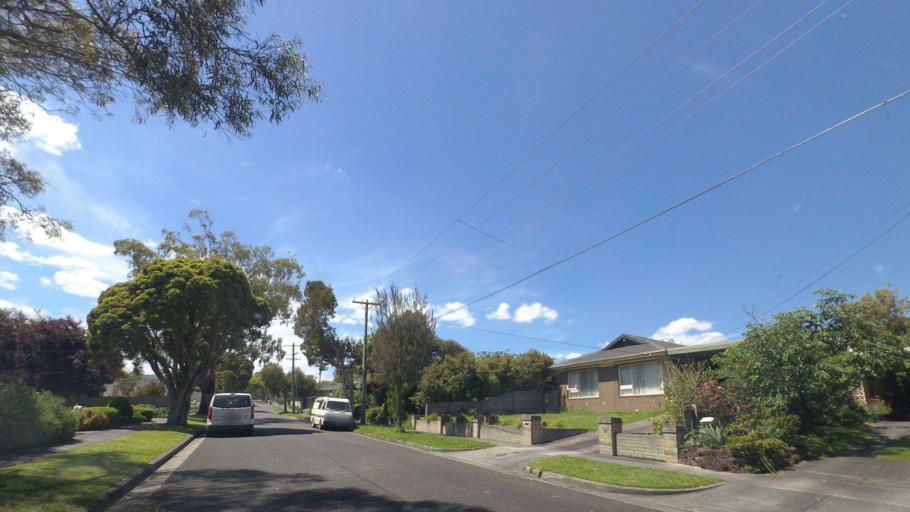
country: AU
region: Victoria
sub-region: Whitehorse
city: Vermont
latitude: -37.8454
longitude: 145.1961
